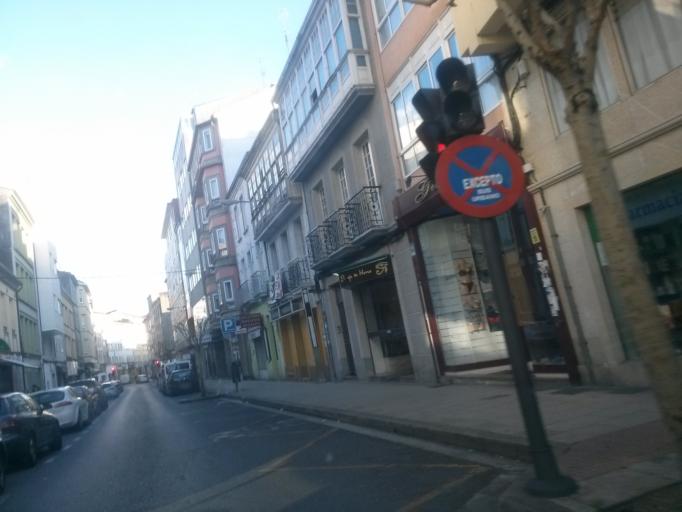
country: ES
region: Galicia
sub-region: Provincia de Lugo
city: Lugo
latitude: 43.0164
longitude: -7.5626
